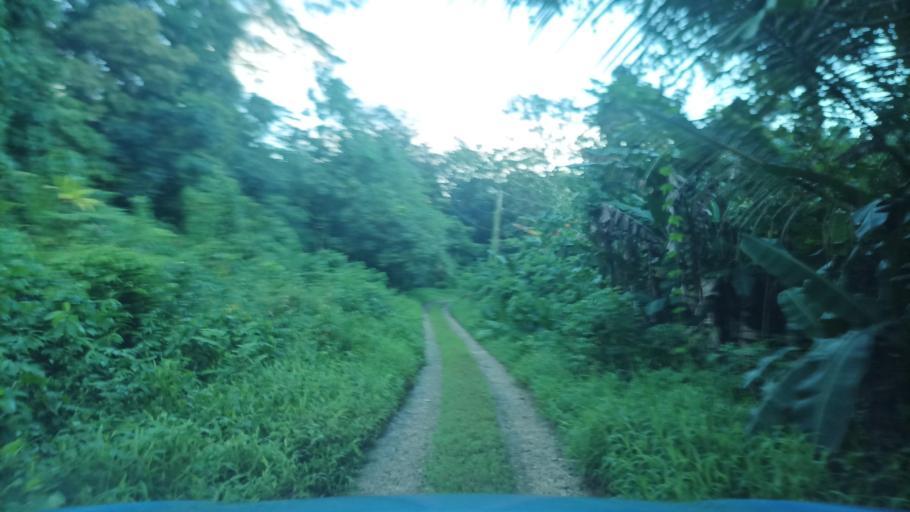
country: FM
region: Pohnpei
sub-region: Kolonia Municipality
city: Kolonia Town
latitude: 6.9746
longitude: 158.1801
